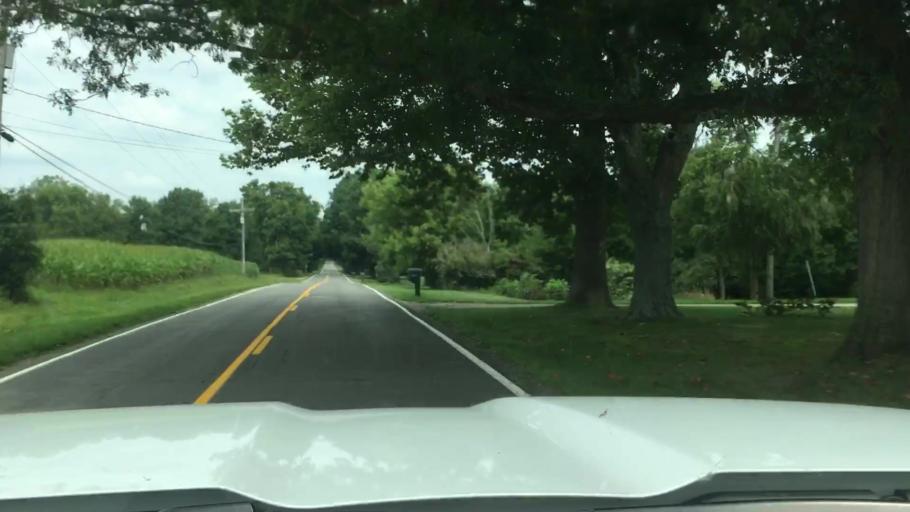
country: US
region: Michigan
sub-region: Ingham County
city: Webberville
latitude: 42.6750
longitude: -84.1891
